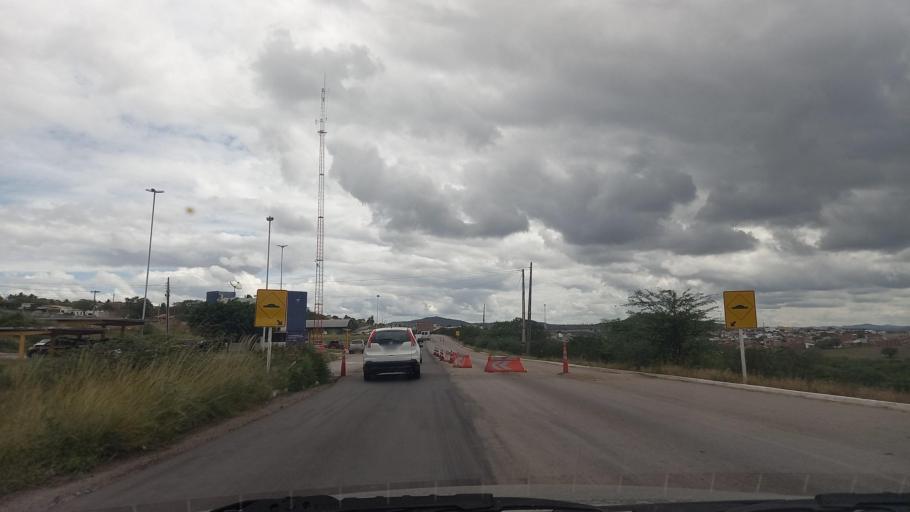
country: BR
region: Pernambuco
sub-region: Caruaru
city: Caruaru
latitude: -8.3291
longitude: -36.1219
